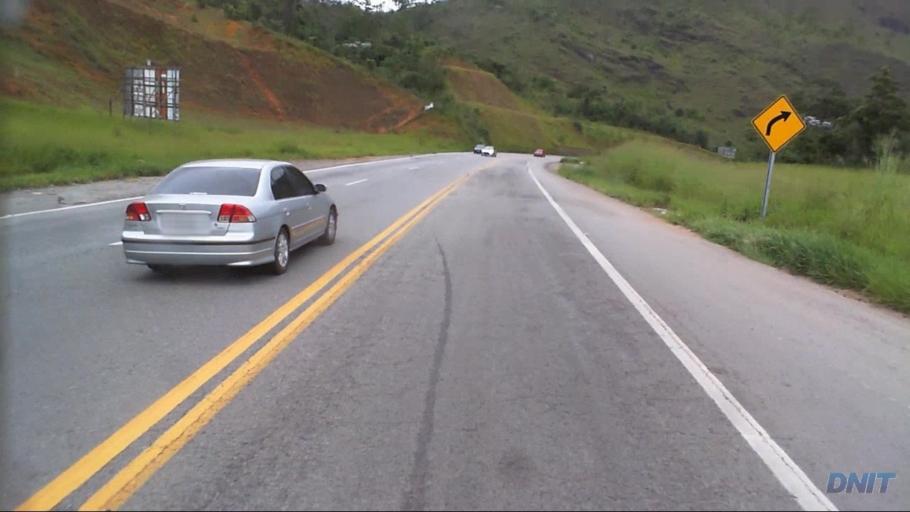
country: BR
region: Minas Gerais
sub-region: Nova Era
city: Nova Era
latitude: -19.6433
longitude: -42.9042
